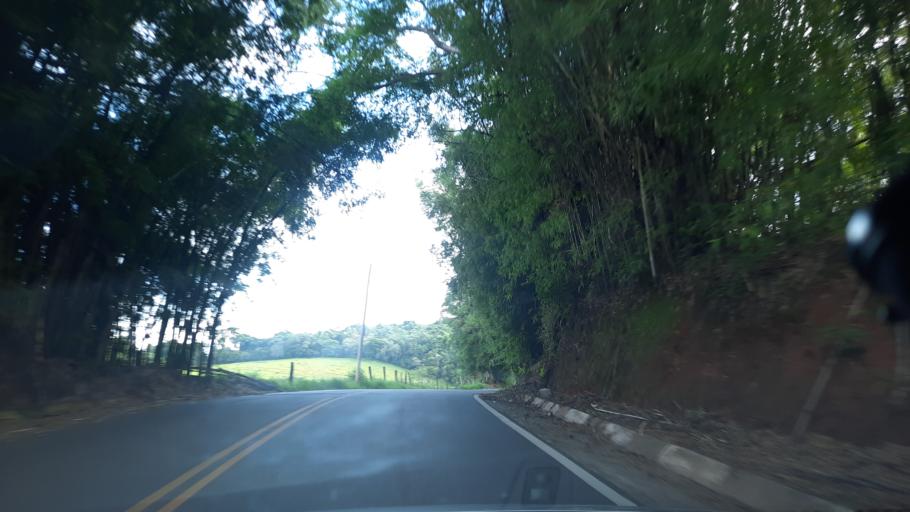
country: BR
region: Sao Paulo
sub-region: Atibaia
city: Atibaia
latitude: -23.0963
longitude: -46.5163
